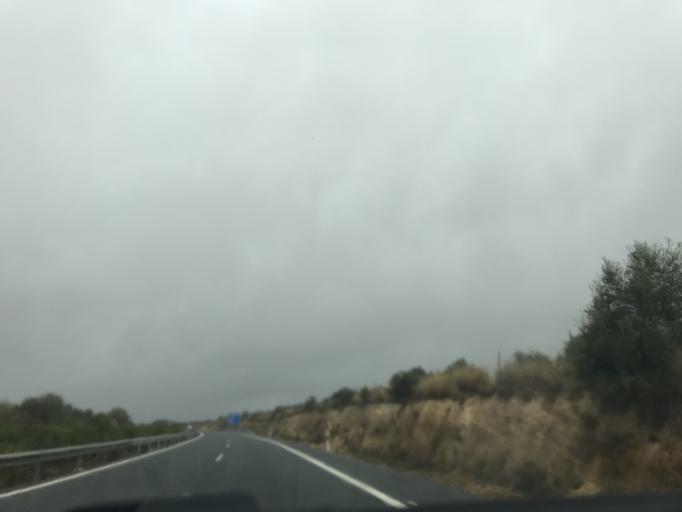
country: ES
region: Andalusia
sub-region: Provincia de Malaga
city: Mollina
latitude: 37.1285
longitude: -4.6818
